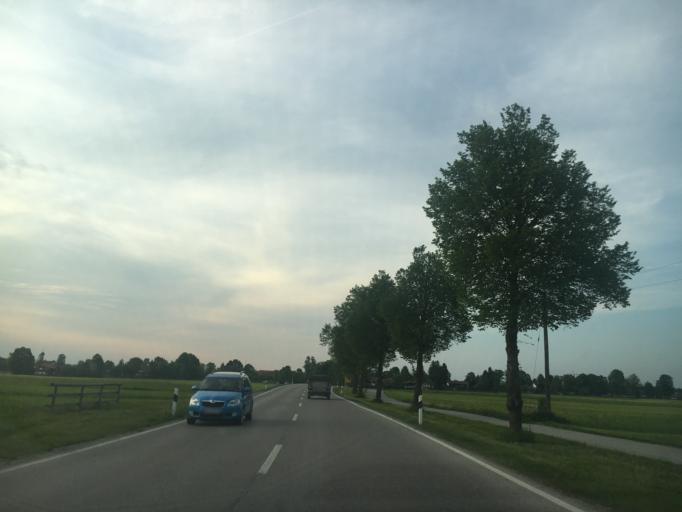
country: DE
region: Bavaria
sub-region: Upper Bavaria
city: Benediktbeuern
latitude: 47.7121
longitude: 11.4133
